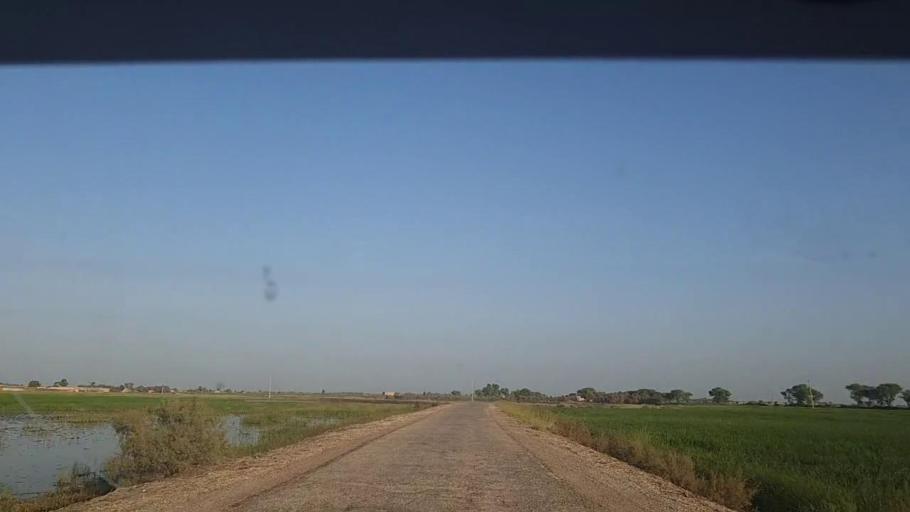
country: PK
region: Sindh
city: Thul
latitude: 28.1849
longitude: 68.8761
